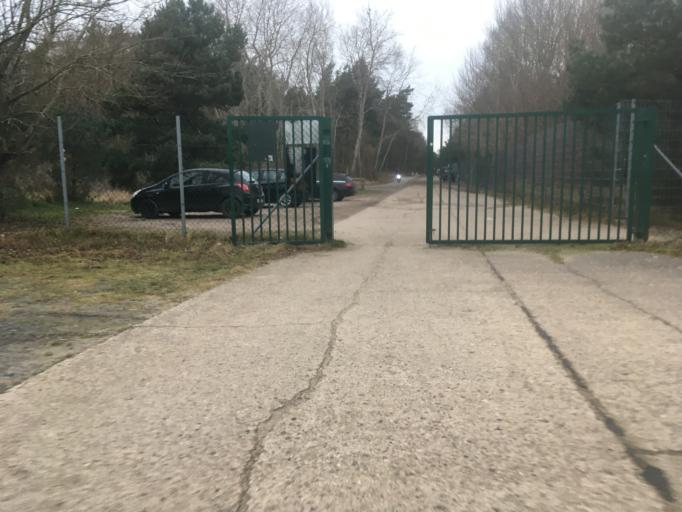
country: DE
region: Mecklenburg-Vorpommern
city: Ostseebad Binz
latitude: 54.4561
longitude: 13.5676
